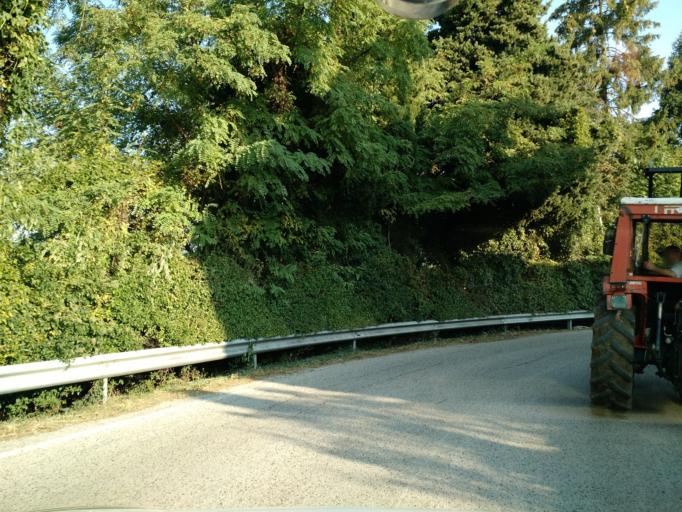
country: IT
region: Veneto
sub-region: Provincia di Vicenza
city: Salcedo
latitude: 45.7603
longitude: 11.5661
